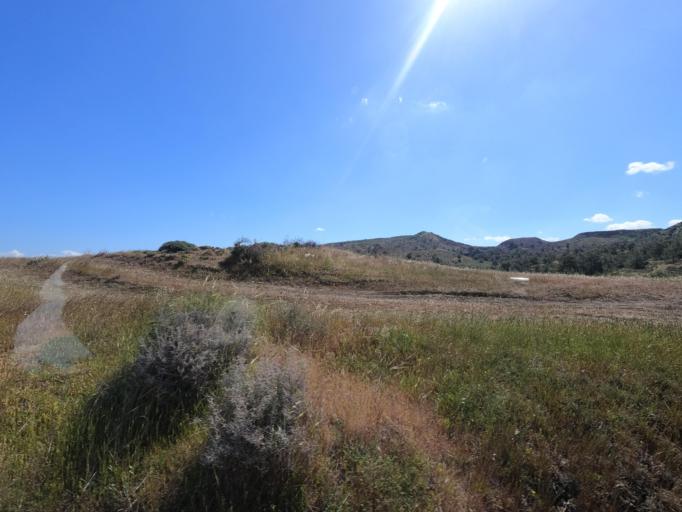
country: CY
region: Lefkosia
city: Peristerona
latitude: 35.0647
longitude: 33.0584
